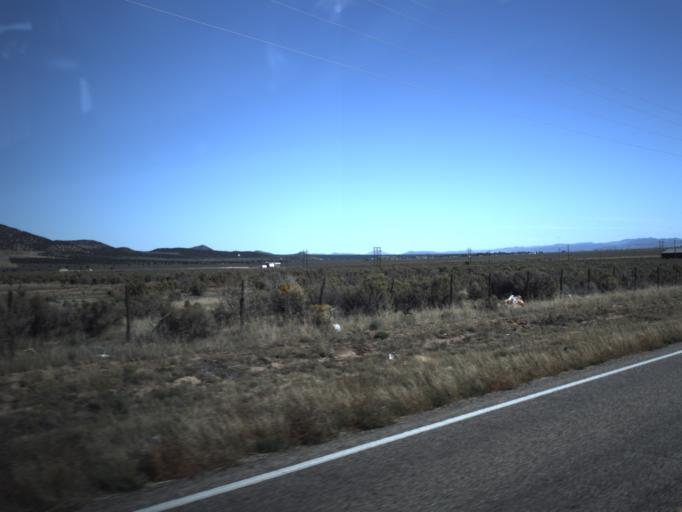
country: US
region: Utah
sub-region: Iron County
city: Cedar City
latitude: 37.6569
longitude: -113.2200
